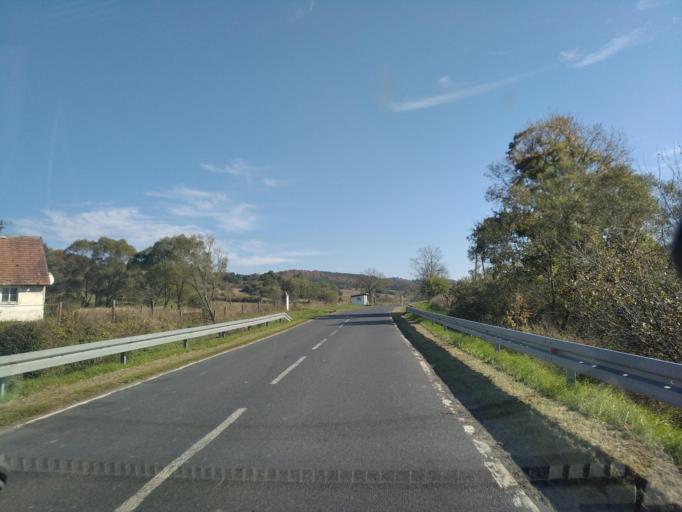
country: PL
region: Subcarpathian Voivodeship
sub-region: Powiat sanocki
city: Bukowsko
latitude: 49.4148
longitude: 21.9683
